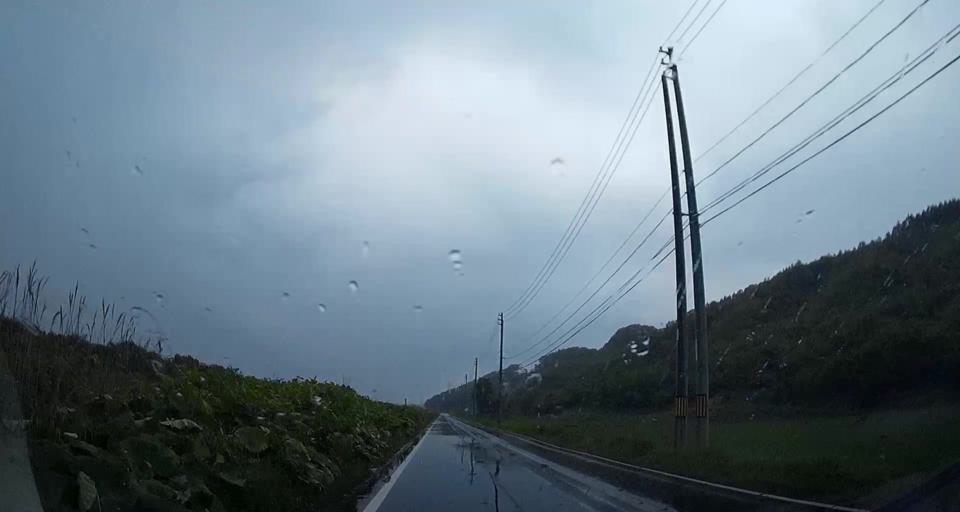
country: JP
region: Hokkaido
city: Chitose
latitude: 42.7440
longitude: 141.9064
